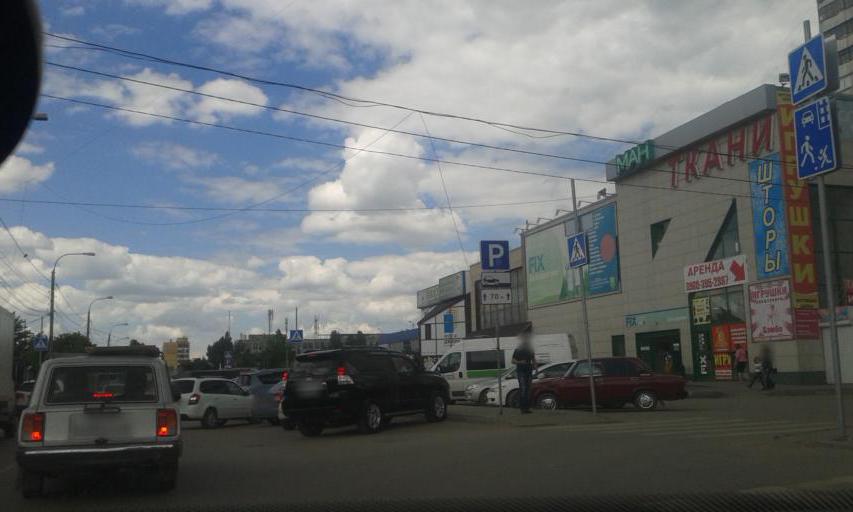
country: RU
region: Volgograd
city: Volgograd
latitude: 48.7575
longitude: 44.5016
